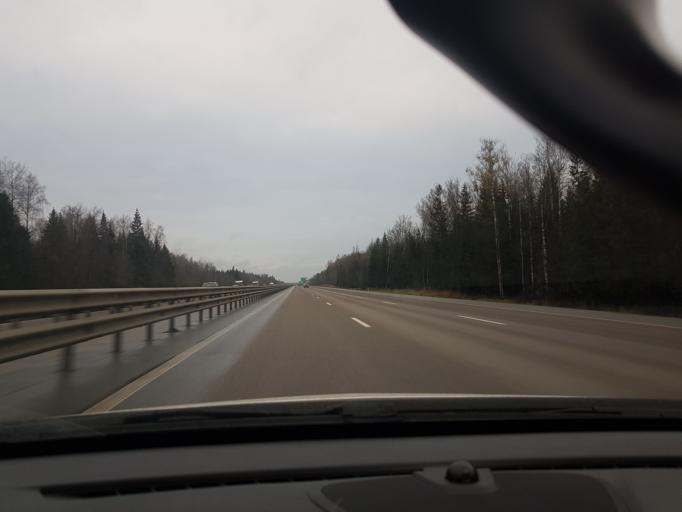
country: RU
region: Moskovskaya
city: Kostrovo
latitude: 55.9069
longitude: 36.6201
